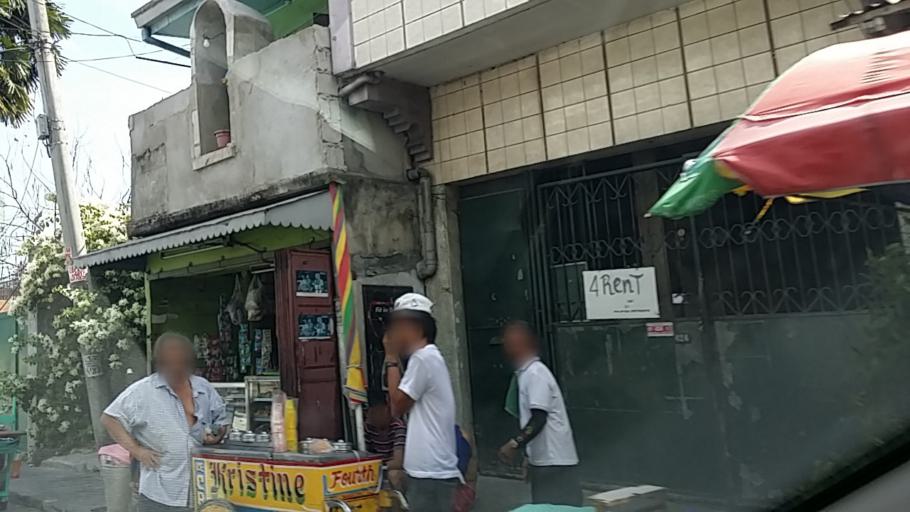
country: PH
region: Metro Manila
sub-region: Mandaluyong
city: Mandaluyong City
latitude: 14.5743
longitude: 121.0338
